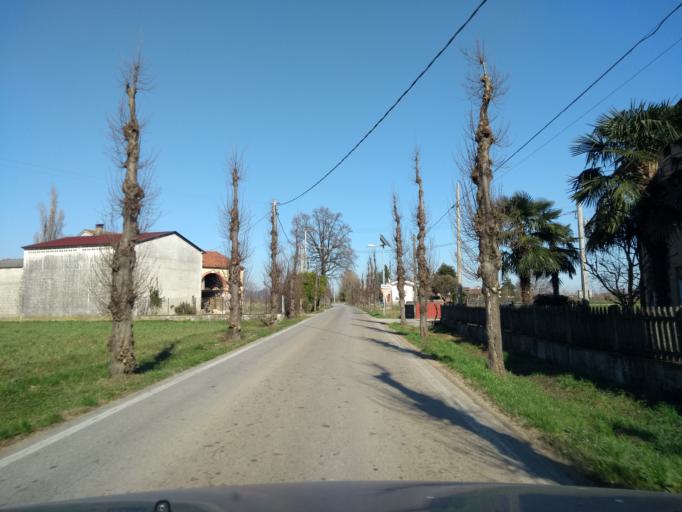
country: IT
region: Veneto
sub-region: Provincia di Padova
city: San Pietro in Gu
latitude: 45.6213
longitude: 11.6602
